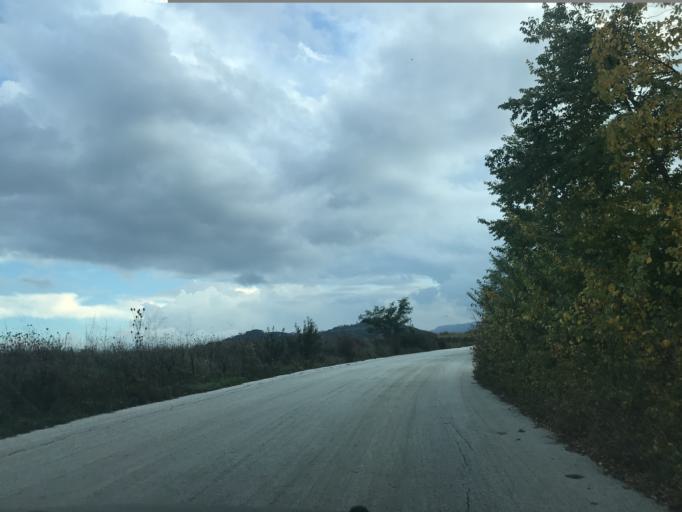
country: IT
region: Molise
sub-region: Provincia di Isernia
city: Bagnoli del Trigno
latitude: 41.6889
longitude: 14.4619
